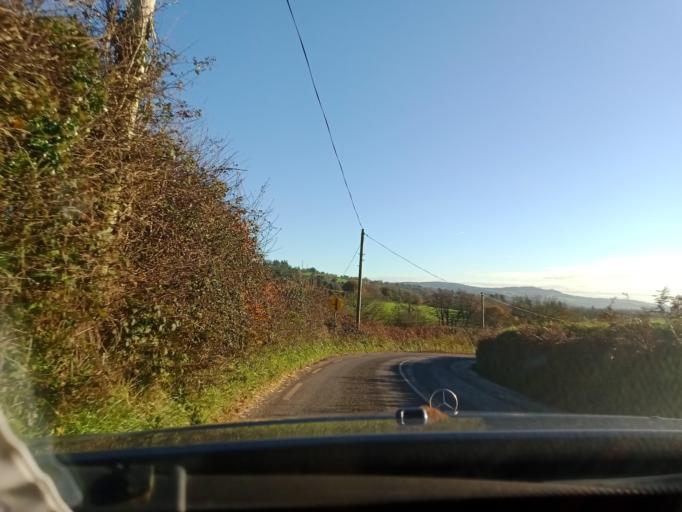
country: IE
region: Leinster
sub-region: Kilkenny
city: Piltown
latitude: 52.3940
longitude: -7.3518
